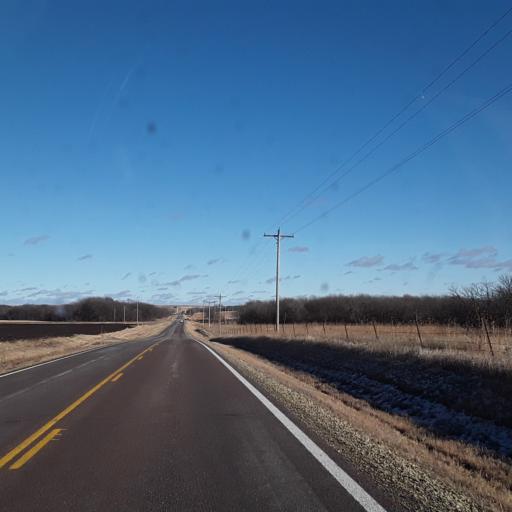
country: US
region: Kansas
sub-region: Cloud County
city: Concordia
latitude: 39.4961
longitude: -97.7475
